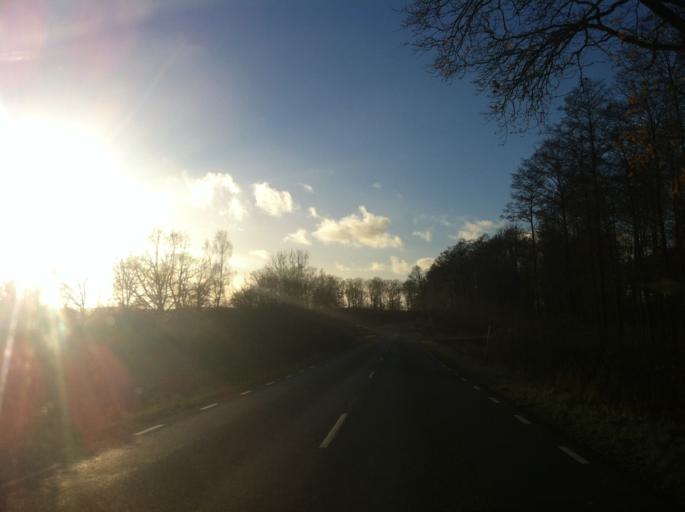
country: SE
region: Skane
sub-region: Ostra Goinge Kommun
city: Knislinge
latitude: 56.1889
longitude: 14.0389
